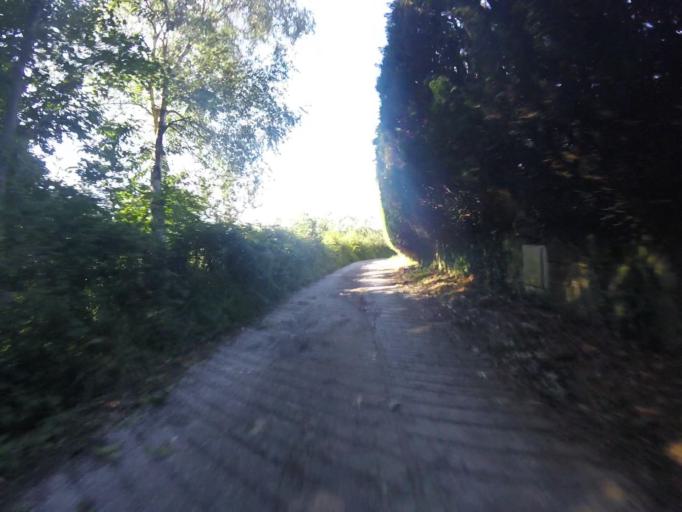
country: ES
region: Basque Country
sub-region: Provincia de Guipuzcoa
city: Irun
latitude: 43.3155
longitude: -1.7767
